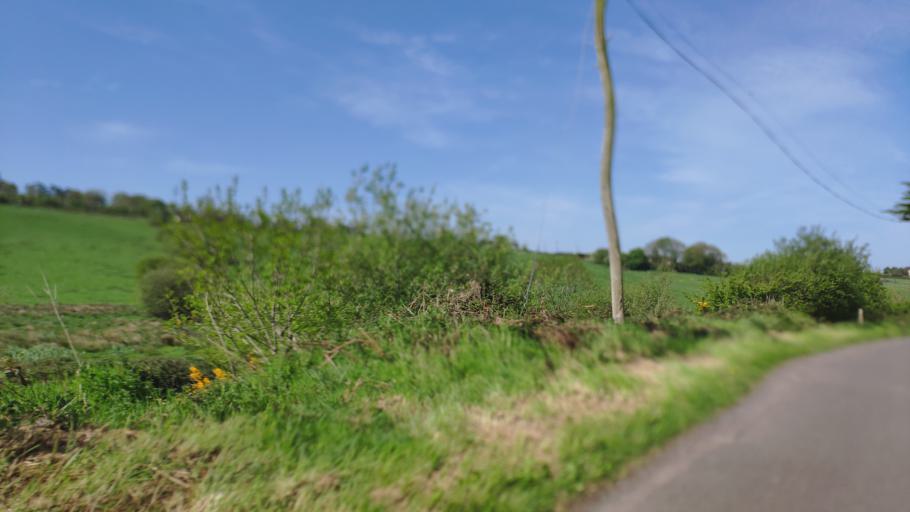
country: IE
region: Munster
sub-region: County Cork
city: Blarney
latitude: 51.9129
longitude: -8.5260
